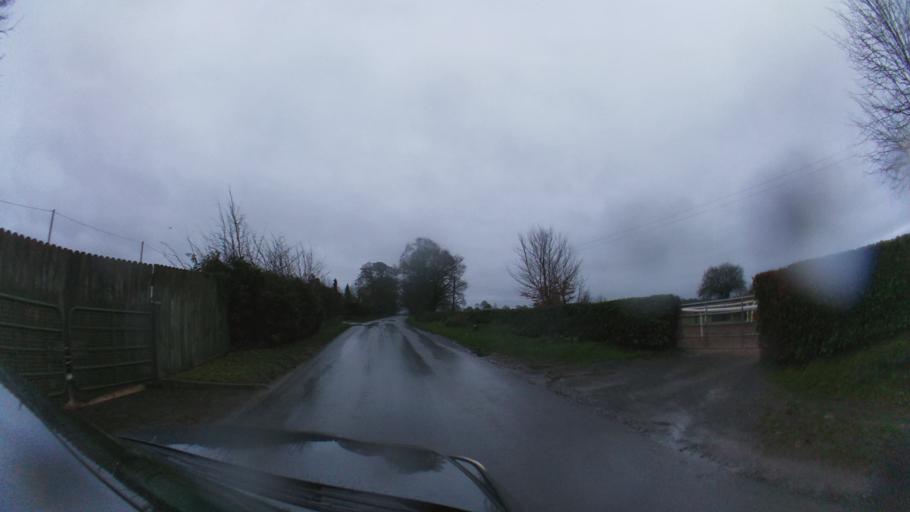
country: IE
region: Leinster
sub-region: County Carlow
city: Bagenalstown
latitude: 52.6652
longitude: -6.9954
